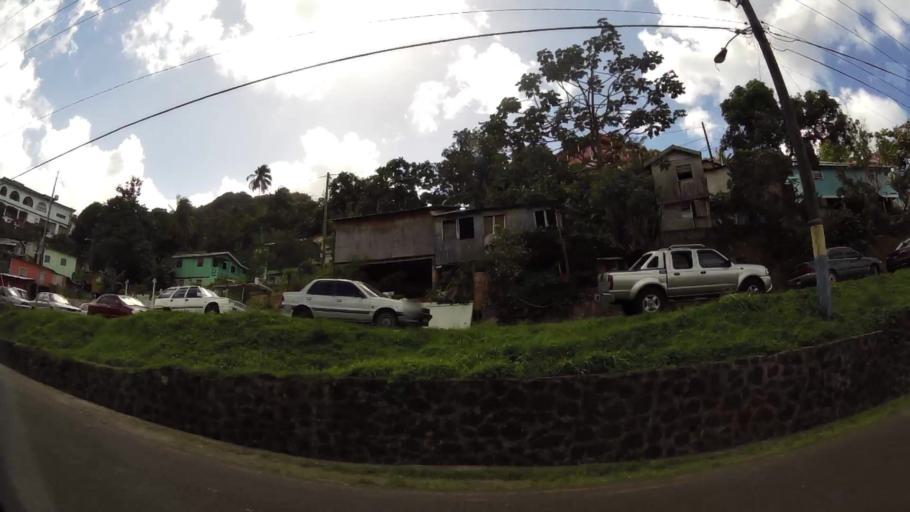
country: LC
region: Castries Quarter
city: Castries
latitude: 14.0085
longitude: -60.9936
